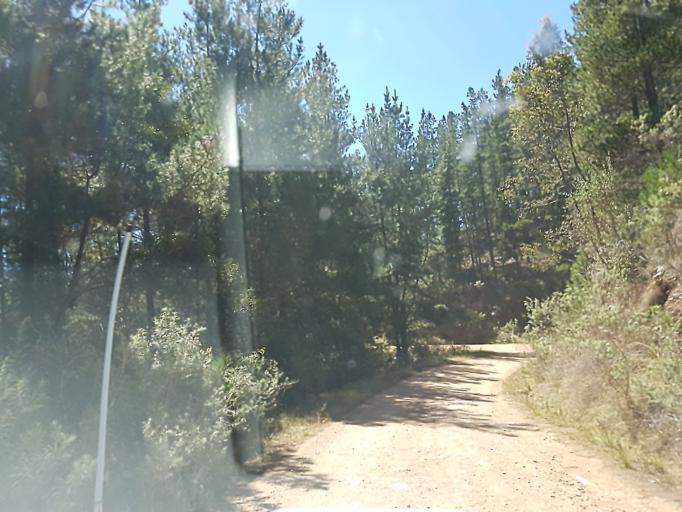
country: AU
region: Victoria
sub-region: Alpine
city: Mount Beauty
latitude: -36.7446
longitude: 146.9591
